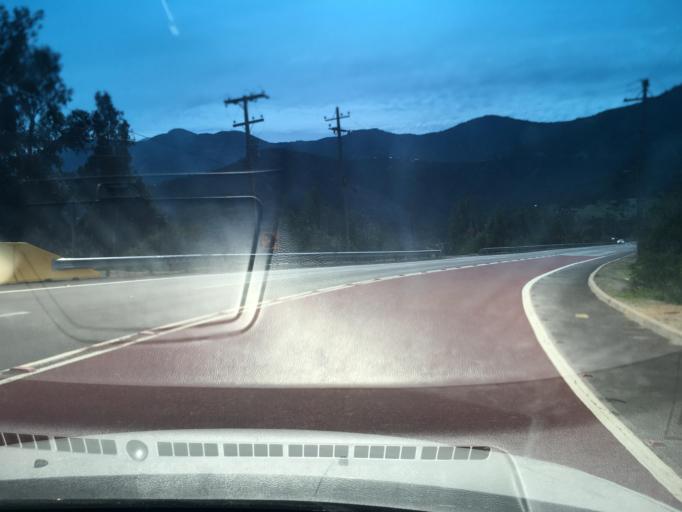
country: CL
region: Valparaiso
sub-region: Provincia de San Felipe
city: Llaillay
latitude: -33.0628
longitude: -71.0314
